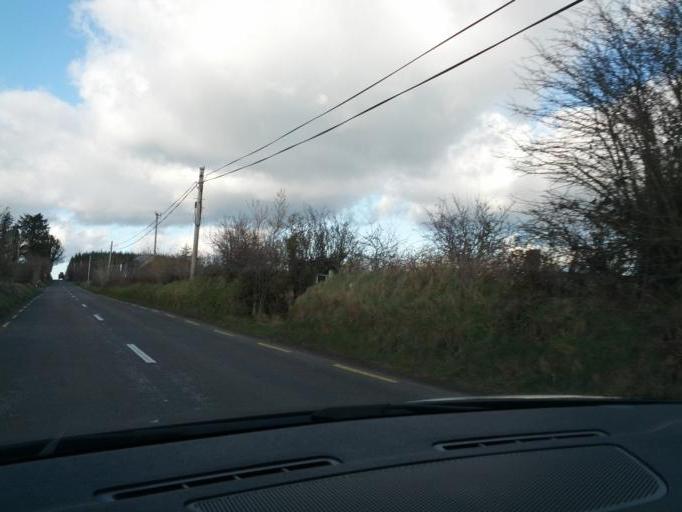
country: IE
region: Connaught
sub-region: Roscommon
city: Castlerea
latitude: 53.6539
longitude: -8.5148
